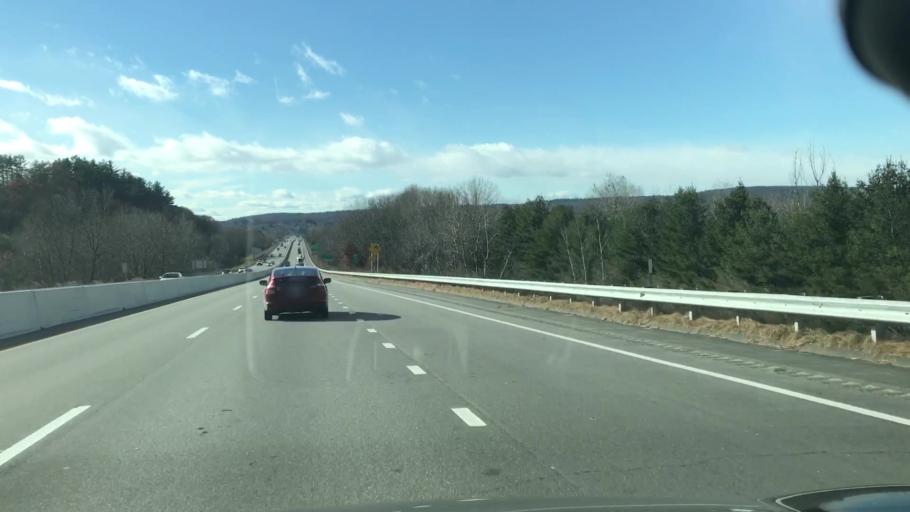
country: US
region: New Hampshire
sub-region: Merrimack County
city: Concord
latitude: 43.2234
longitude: -71.5099
